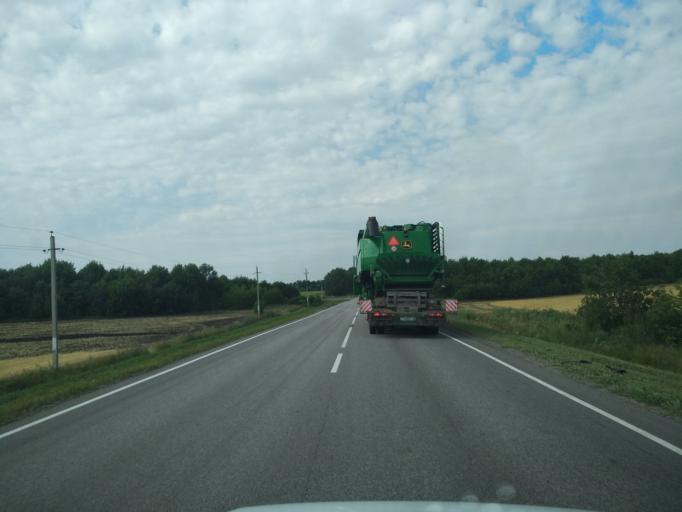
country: RU
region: Voronezj
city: Pereleshinskiy
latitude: 51.8791
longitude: 40.4164
